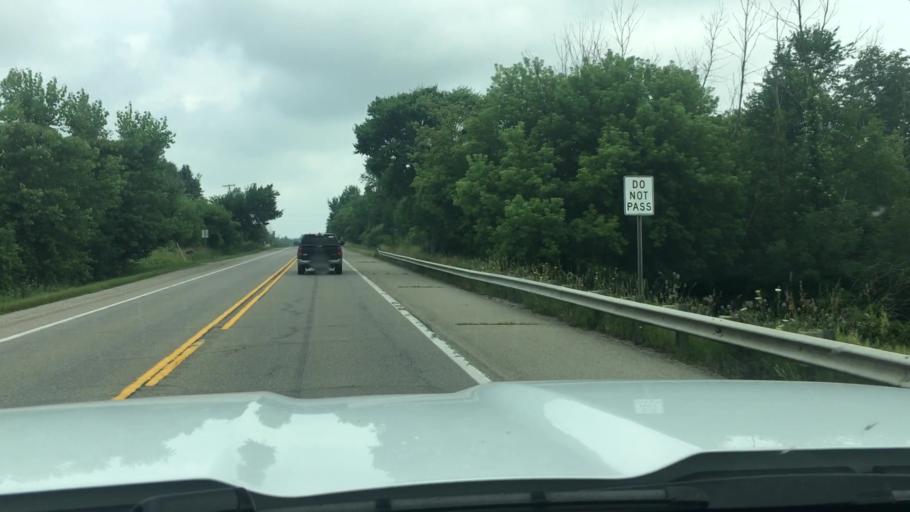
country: US
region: Michigan
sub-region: Lapeer County
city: Imlay City
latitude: 43.0747
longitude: -83.0752
